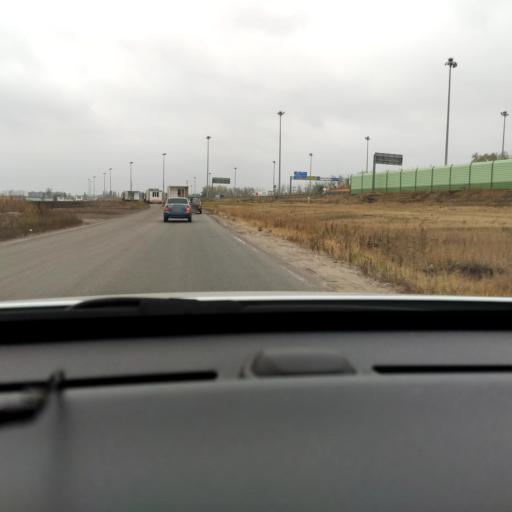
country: RU
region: Voronezj
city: Somovo
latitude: 51.6582
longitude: 39.3038
